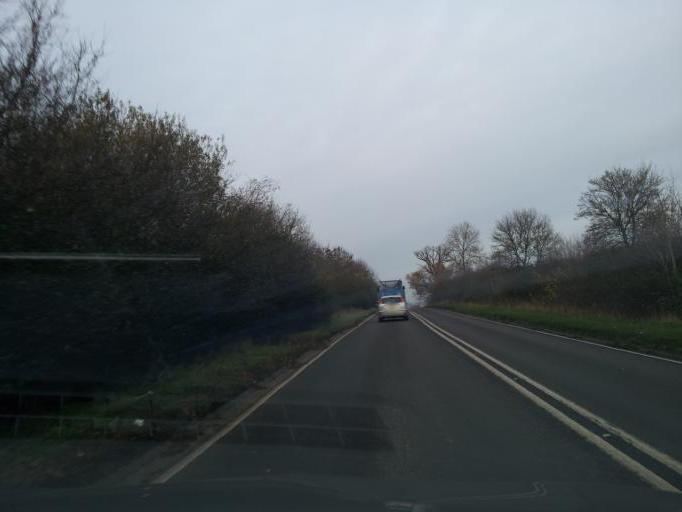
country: GB
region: England
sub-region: Buckinghamshire
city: Stewkley
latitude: 51.8653
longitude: -0.7610
